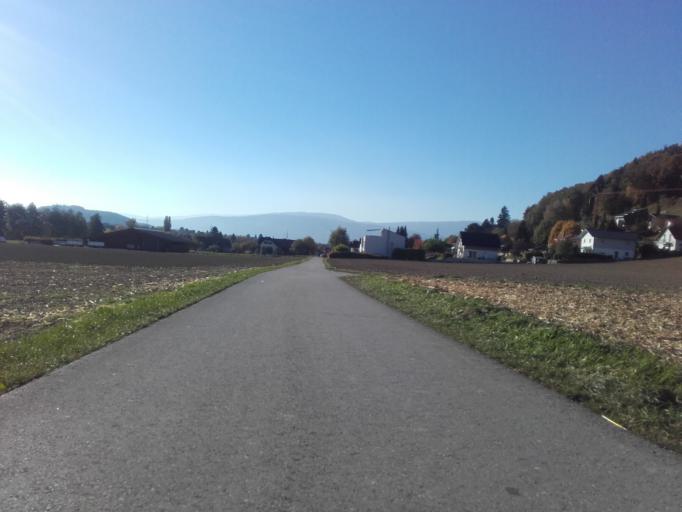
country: CH
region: Bern
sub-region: Biel/Bienne District
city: Meinisberg
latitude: 47.1189
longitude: 7.3501
